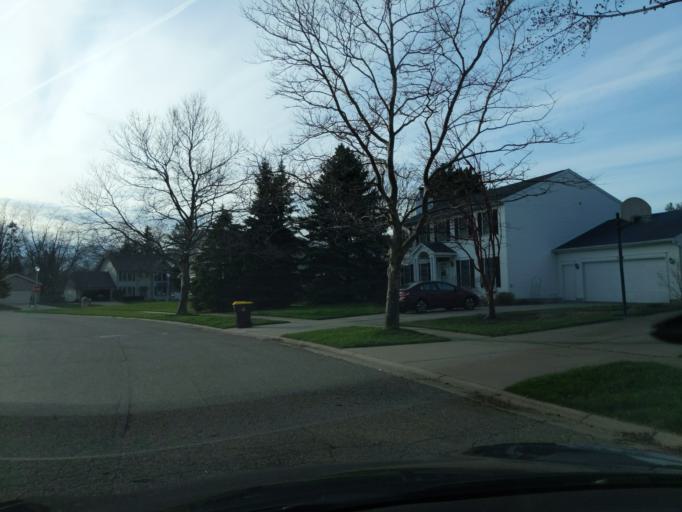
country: US
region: Michigan
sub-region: Eaton County
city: Waverly
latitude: 42.7240
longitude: -84.6260
